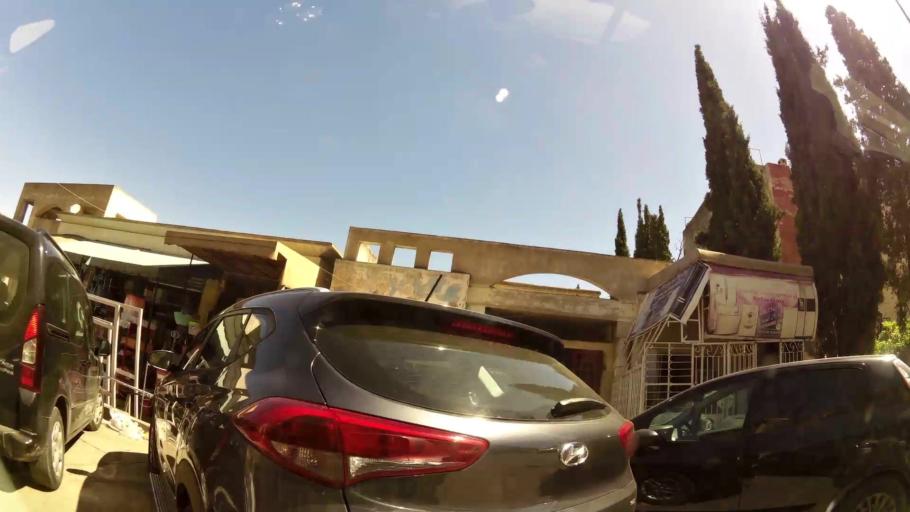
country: MA
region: Meknes-Tafilalet
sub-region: Meknes
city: Meknes
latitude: 33.9070
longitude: -5.5270
